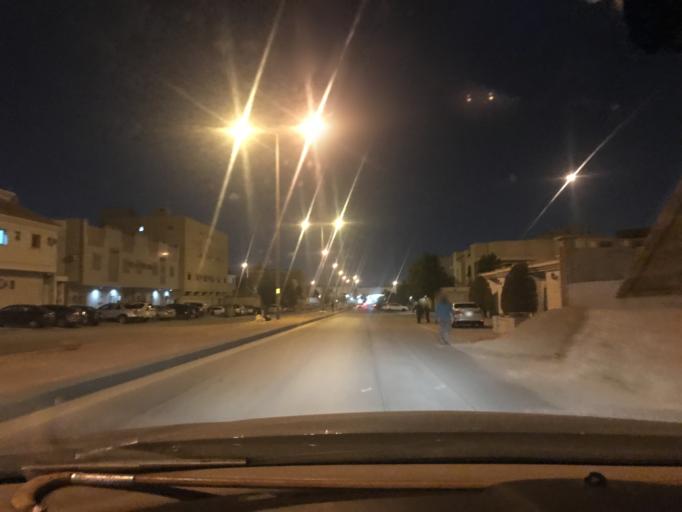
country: SA
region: Ar Riyad
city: Riyadh
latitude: 24.7578
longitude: 46.7473
